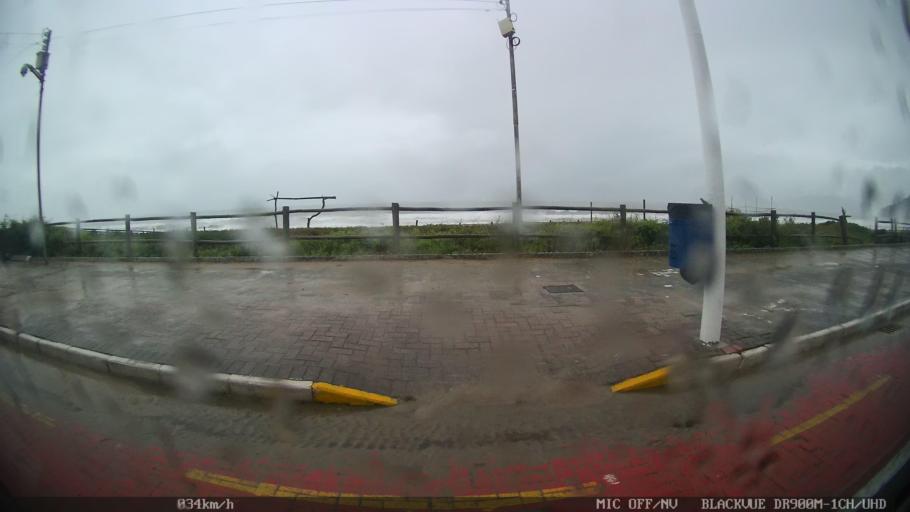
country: BR
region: Santa Catarina
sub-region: Balneario Camboriu
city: Balneario Camboriu
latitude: -26.9497
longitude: -48.6293
